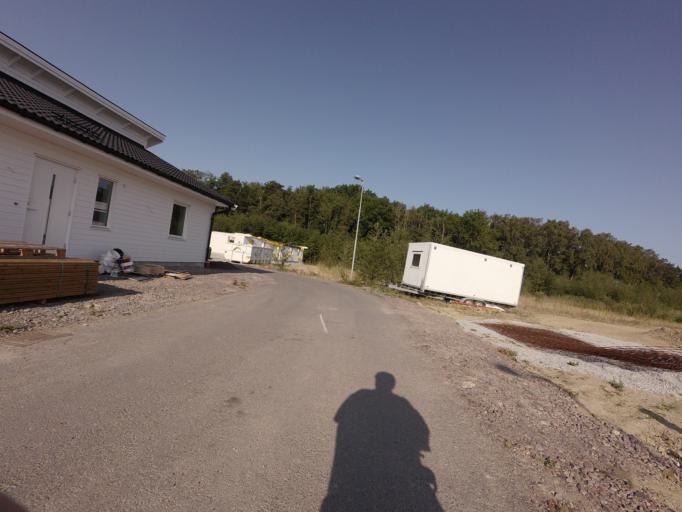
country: SE
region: Skane
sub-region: Landskrona
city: Asmundtorp
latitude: 55.8457
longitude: 12.9209
